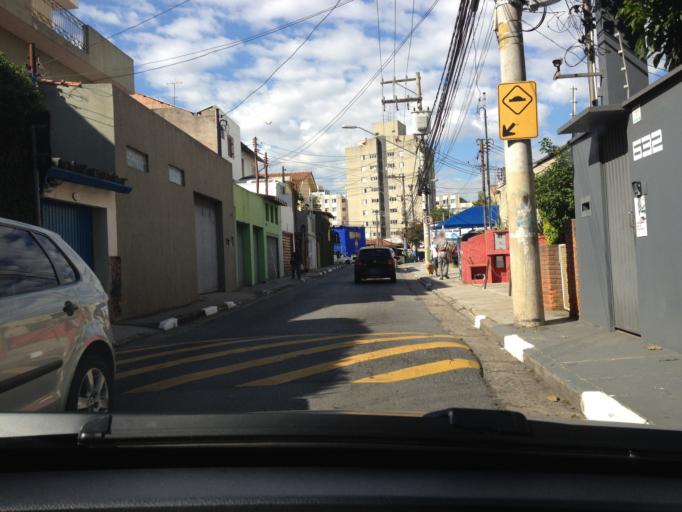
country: BR
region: Sao Paulo
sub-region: Sao Paulo
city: Sao Paulo
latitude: -23.5524
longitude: -46.6956
